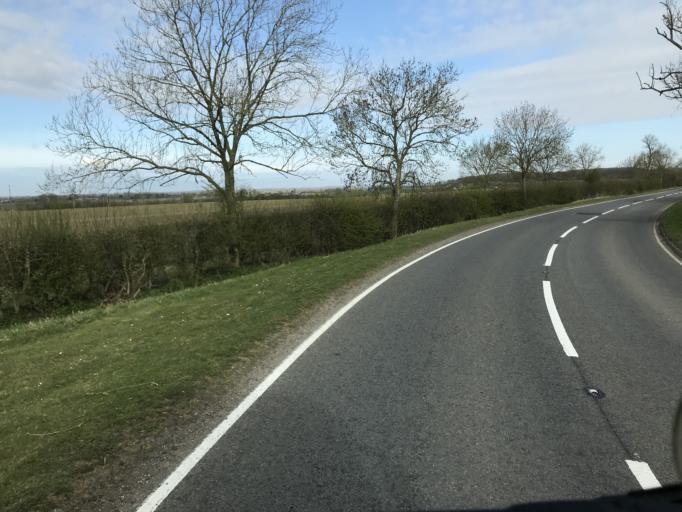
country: GB
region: England
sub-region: Lincolnshire
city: Market Rasen
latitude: 53.3950
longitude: -0.4180
